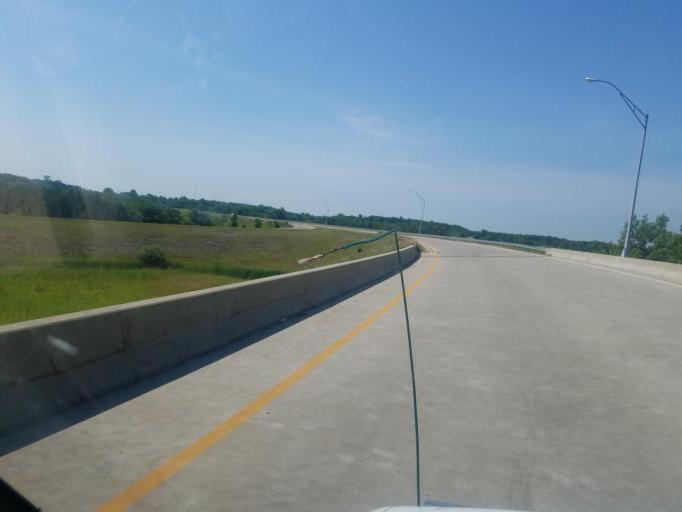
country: US
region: Ohio
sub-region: Union County
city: Marysville
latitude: 40.2412
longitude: -83.4022
